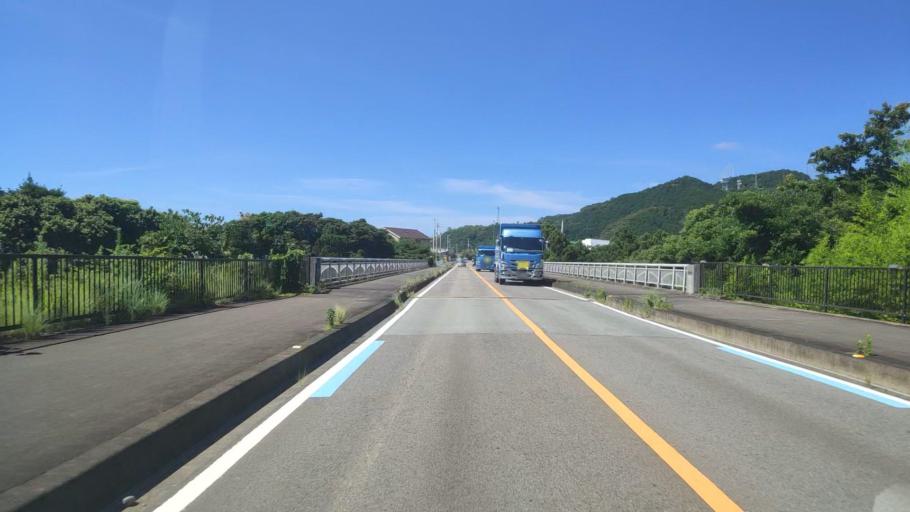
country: JP
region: Wakayama
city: Shingu
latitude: 33.7076
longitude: 135.9949
